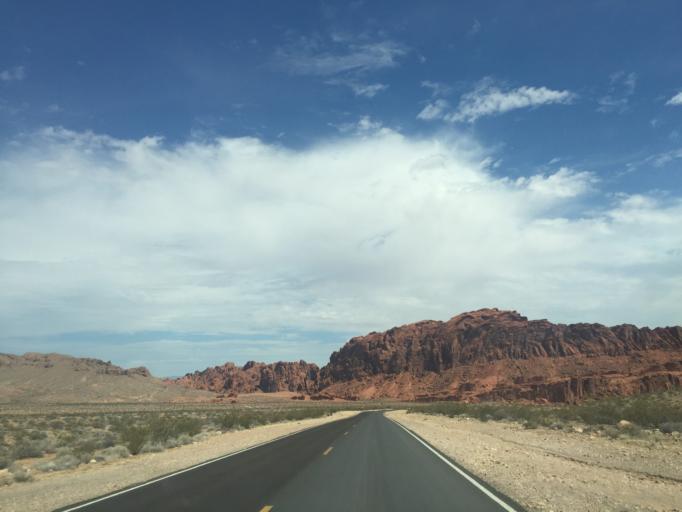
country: US
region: Nevada
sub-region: Clark County
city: Moapa Valley
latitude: 36.4223
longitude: -114.5436
